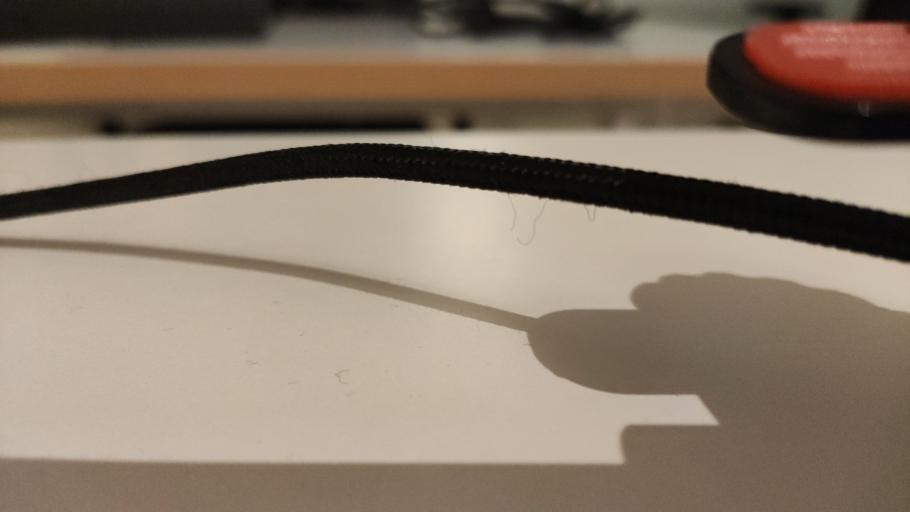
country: RU
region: Moskovskaya
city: Orekhovo-Zuyevo
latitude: 55.8046
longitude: 38.9709
